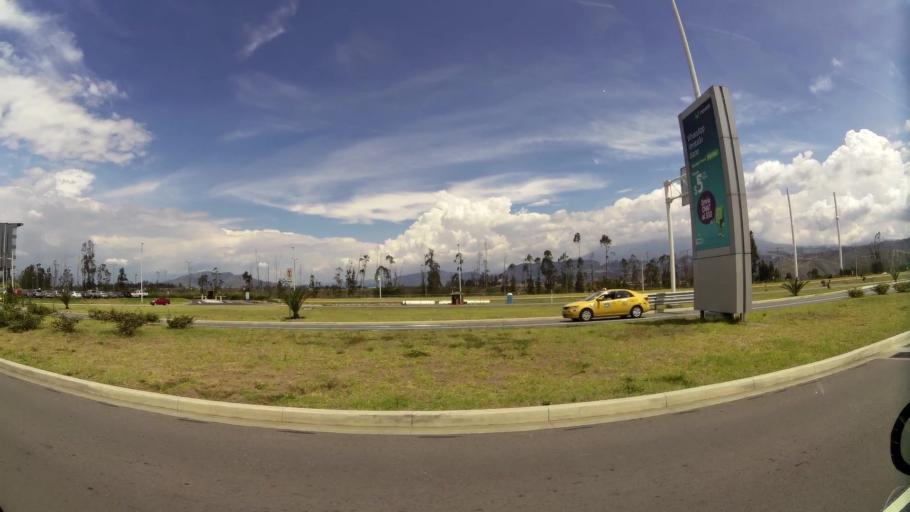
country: EC
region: Pichincha
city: Quito
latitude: -0.1300
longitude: -78.3601
